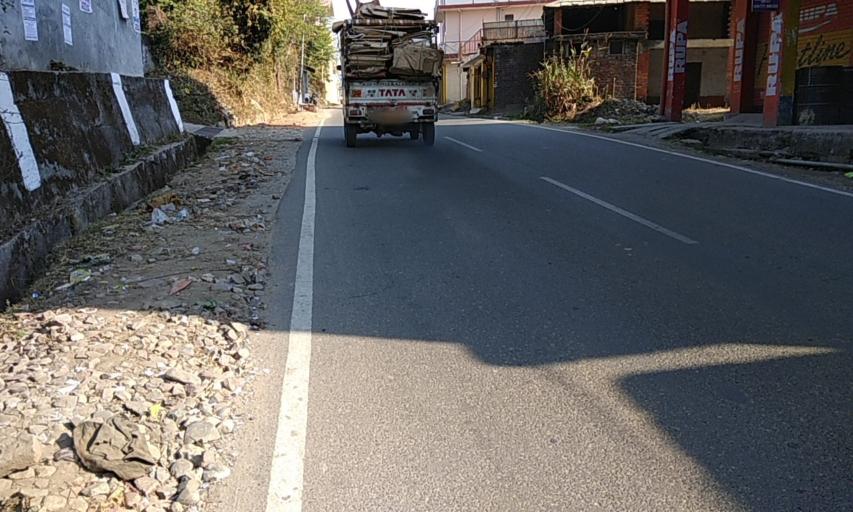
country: IN
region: Himachal Pradesh
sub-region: Kangra
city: Palampur
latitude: 32.1136
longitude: 76.5270
